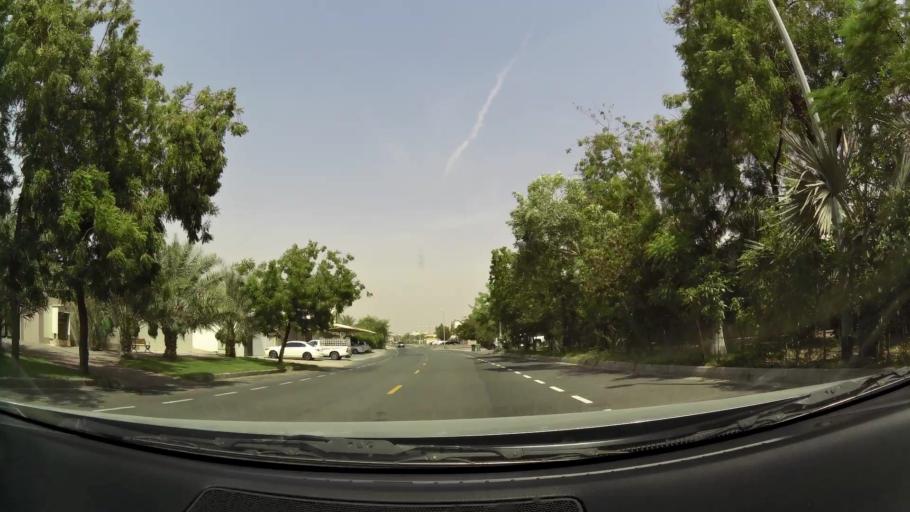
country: AE
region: Ash Shariqah
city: Sharjah
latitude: 25.2413
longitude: 55.4315
